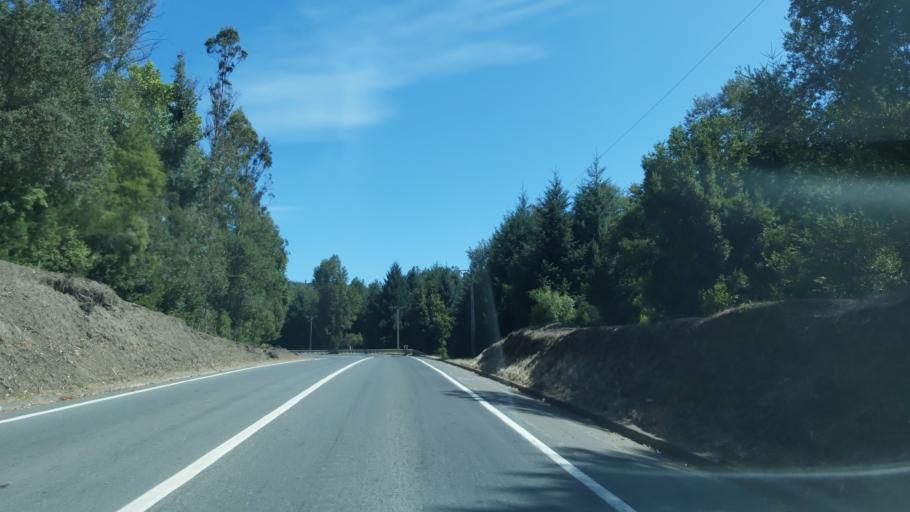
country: CL
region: Biobio
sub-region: Provincia de Concepcion
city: Lota
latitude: -37.1229
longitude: -72.9861
